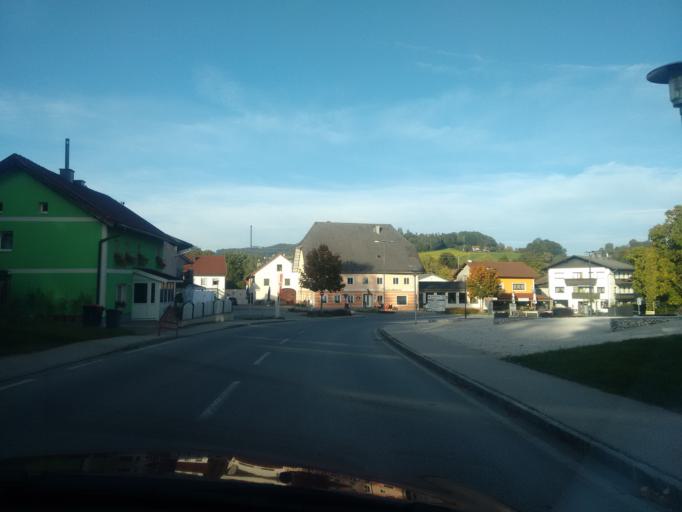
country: AT
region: Upper Austria
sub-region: Politischer Bezirk Vocklabruck
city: Manning
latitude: 48.0959
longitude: 13.6584
